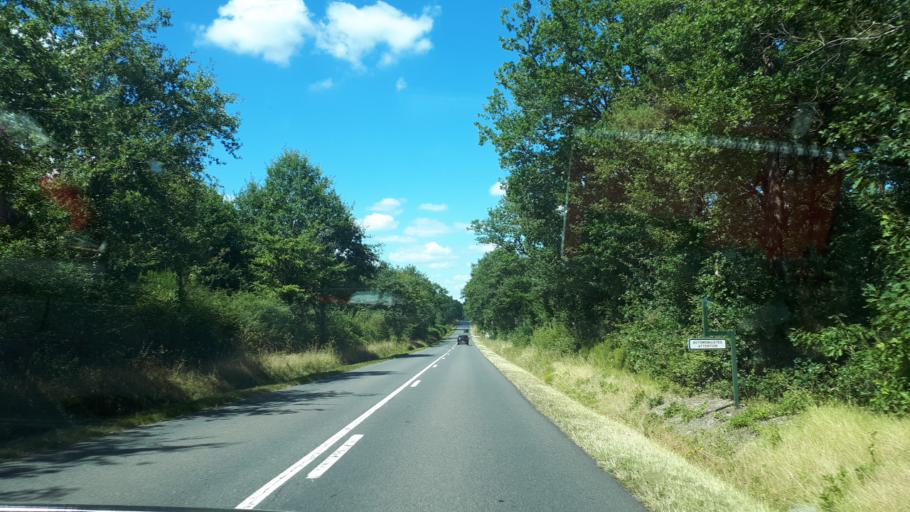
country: FR
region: Centre
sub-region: Departement du Loir-et-Cher
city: Saint-Viatre
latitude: 47.5746
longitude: 1.9616
